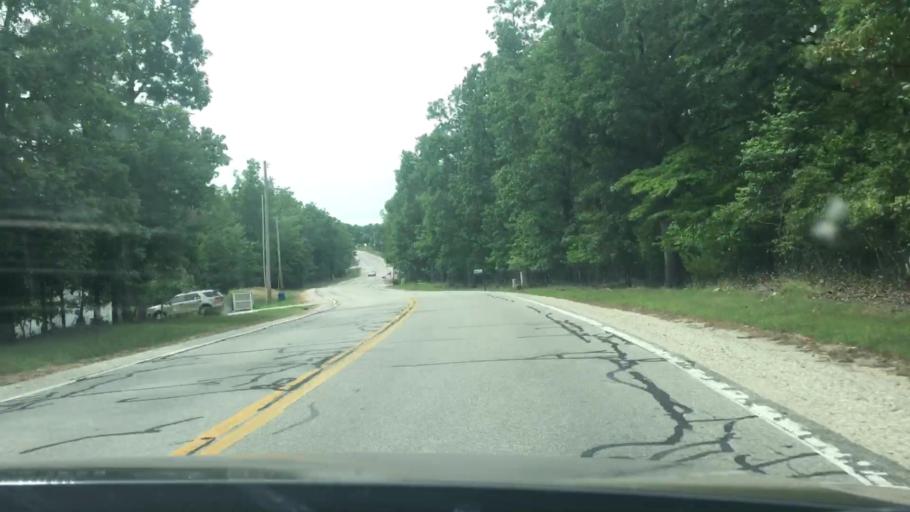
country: US
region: Missouri
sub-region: Camden County
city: Four Seasons
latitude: 38.2060
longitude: -92.7015
